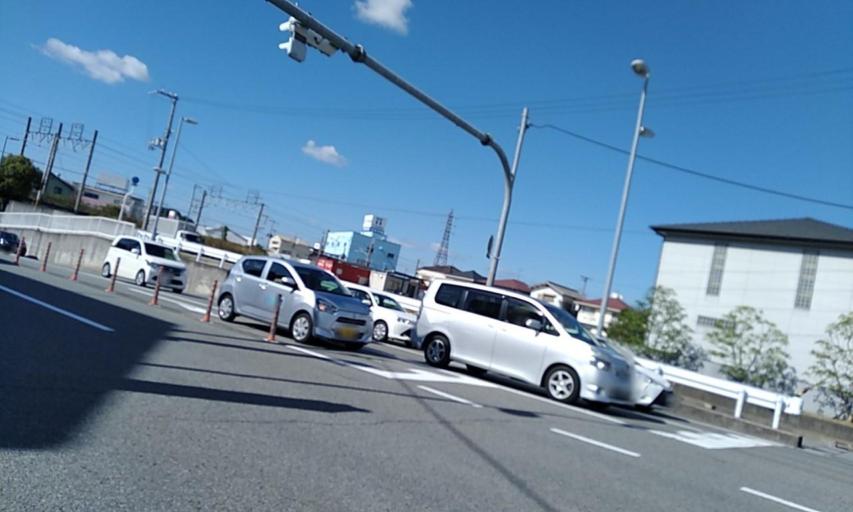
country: JP
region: Wakayama
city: Wakayama-shi
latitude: 34.2009
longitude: 135.1881
